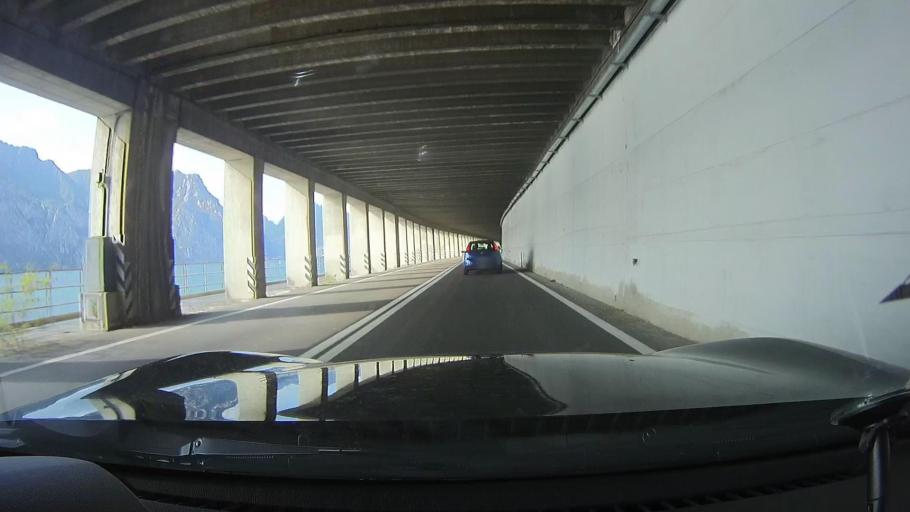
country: IT
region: Trentino-Alto Adige
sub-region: Provincia di Trento
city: Torbole sul Garda
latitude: 45.8188
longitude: 10.8548
